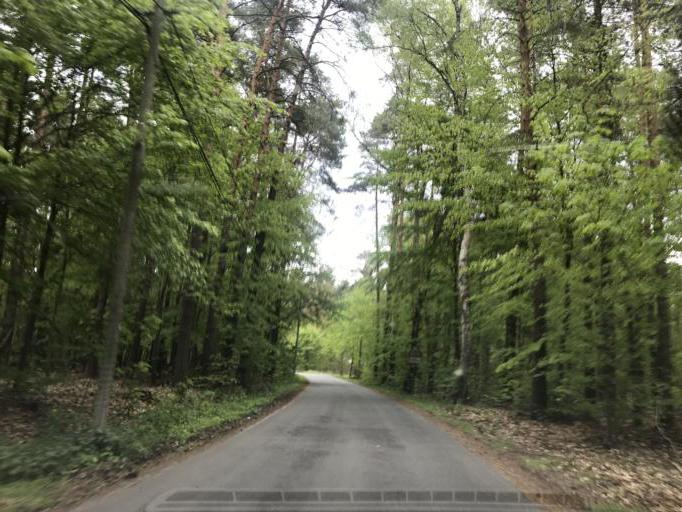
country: DE
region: Brandenburg
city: Rheinsberg
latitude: 53.0980
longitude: 12.8469
